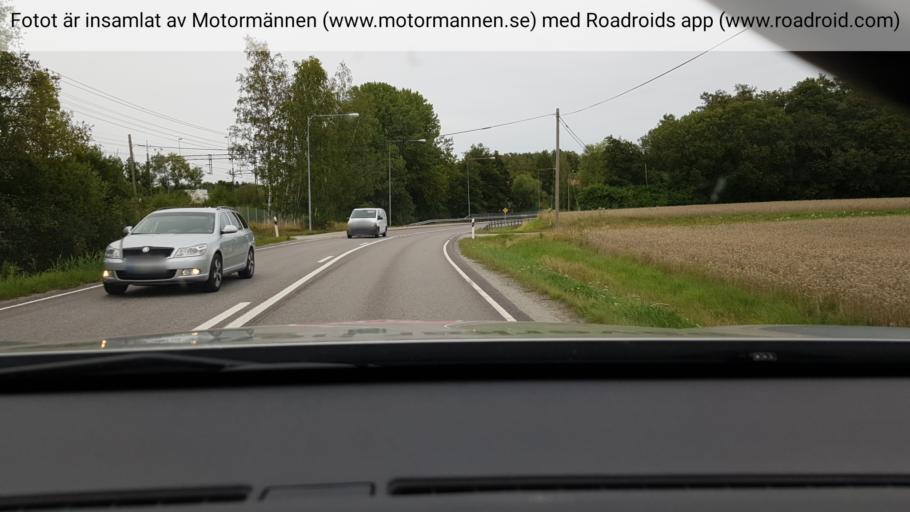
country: SE
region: Stockholm
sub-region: Sodertalje Kommun
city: Pershagen
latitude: 59.0812
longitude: 17.5481
